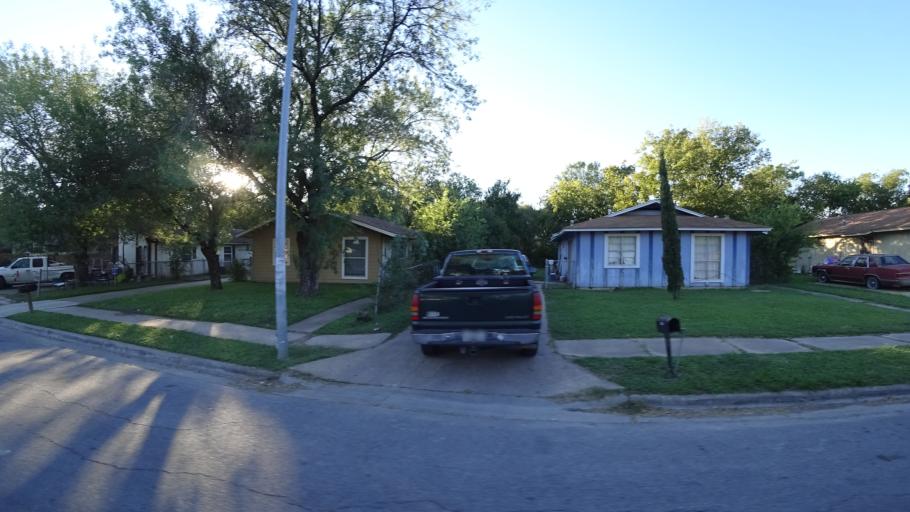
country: US
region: Texas
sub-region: Travis County
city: Austin
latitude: 30.2336
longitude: -97.7015
